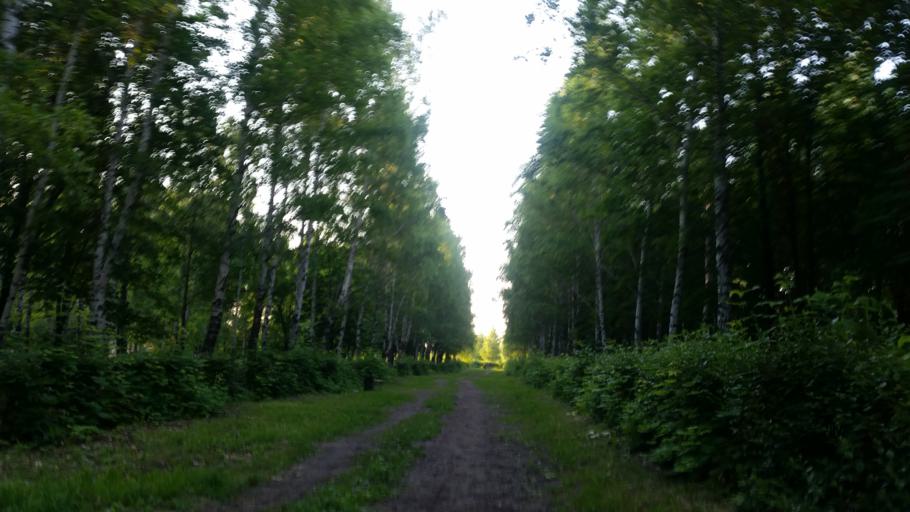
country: RU
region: Ulyanovsk
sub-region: Ulyanovskiy Rayon
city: Ulyanovsk
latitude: 54.3483
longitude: 48.3939
